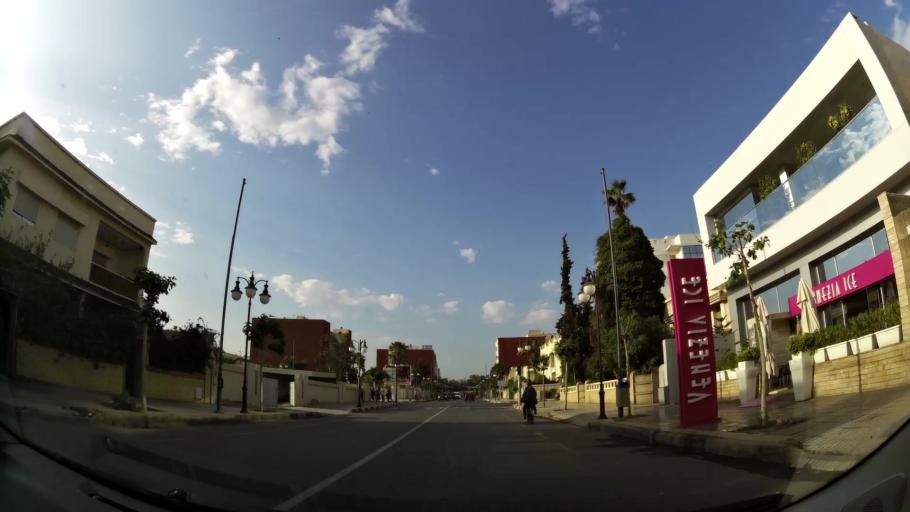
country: MA
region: Oriental
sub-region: Oujda-Angad
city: Oujda
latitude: 34.6745
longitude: -1.9190
